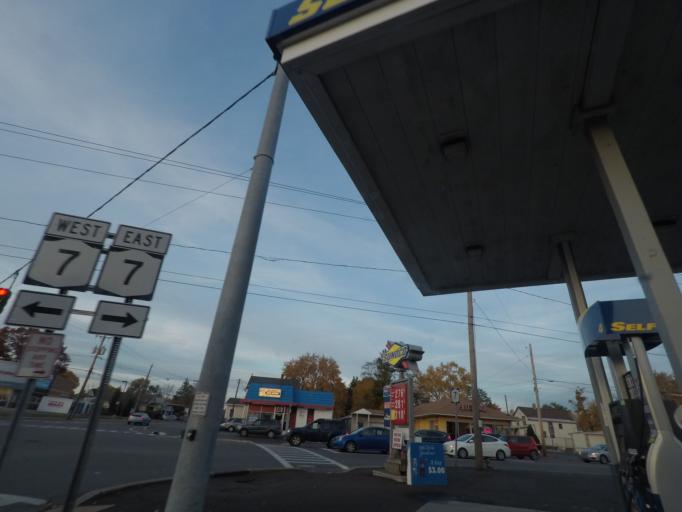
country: US
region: New York
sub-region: Schenectady County
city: Rotterdam
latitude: 42.7866
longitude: -73.9709
